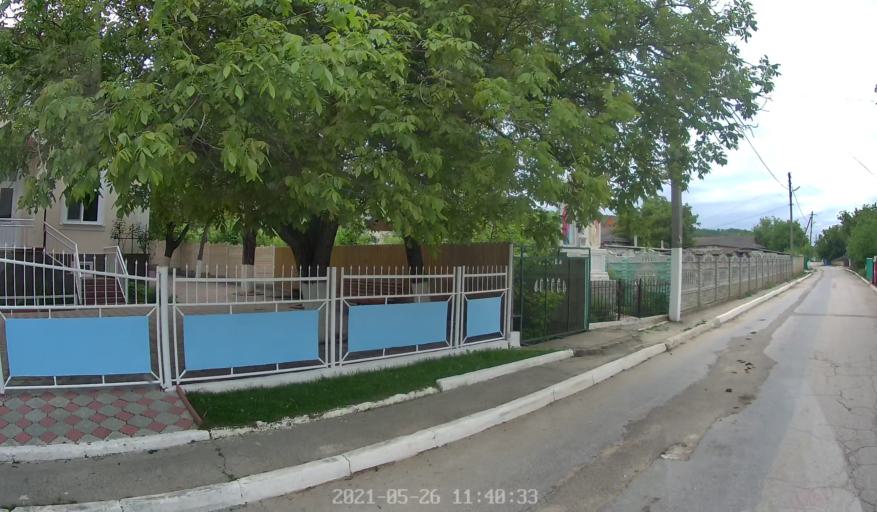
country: MD
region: Hincesti
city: Dancu
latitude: 46.7885
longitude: 28.3550
